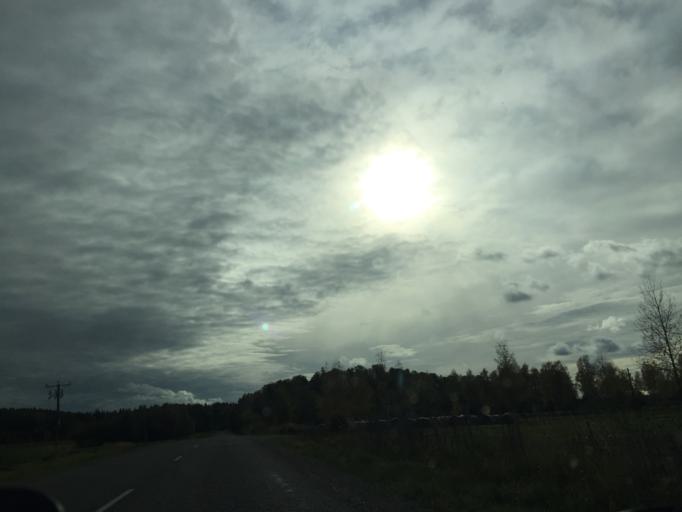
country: LV
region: Auces Novads
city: Auce
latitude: 56.5592
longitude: 23.0192
